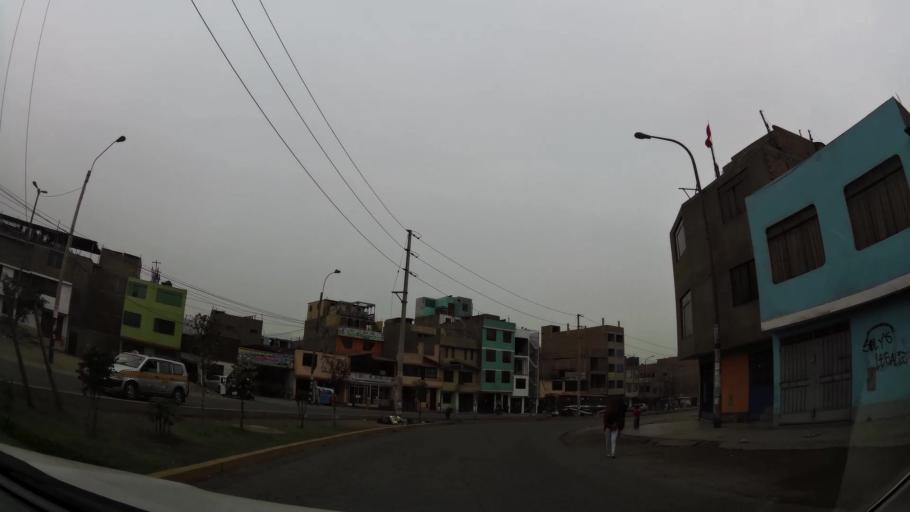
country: PE
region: Lima
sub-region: Lima
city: Independencia
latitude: -11.9559
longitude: -76.9824
